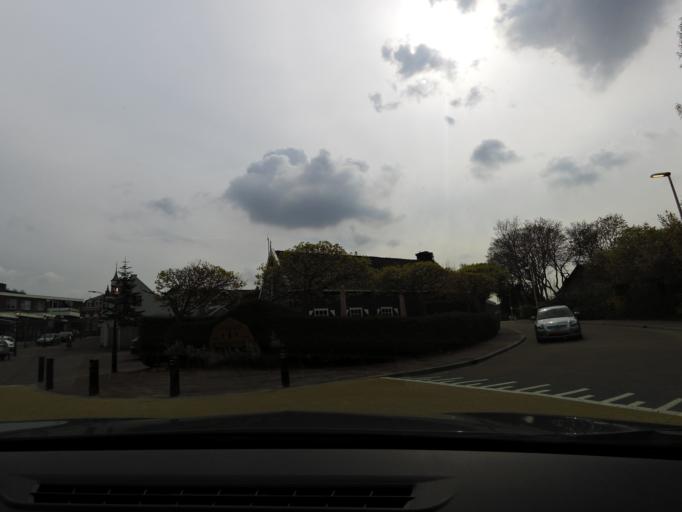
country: NL
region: South Holland
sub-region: Gemeente Albrandswaard
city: Rhoon
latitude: 51.8574
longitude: 4.3885
